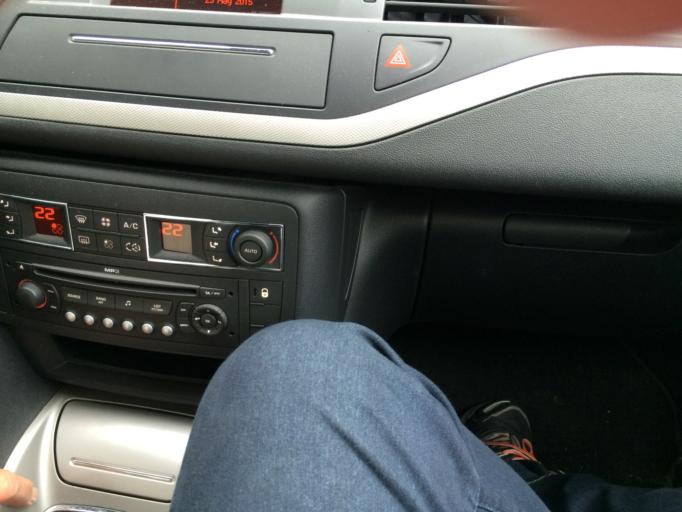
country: DK
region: Central Jutland
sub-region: Arhus Kommune
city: Hjortshoj
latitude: 56.2303
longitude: 10.2986
